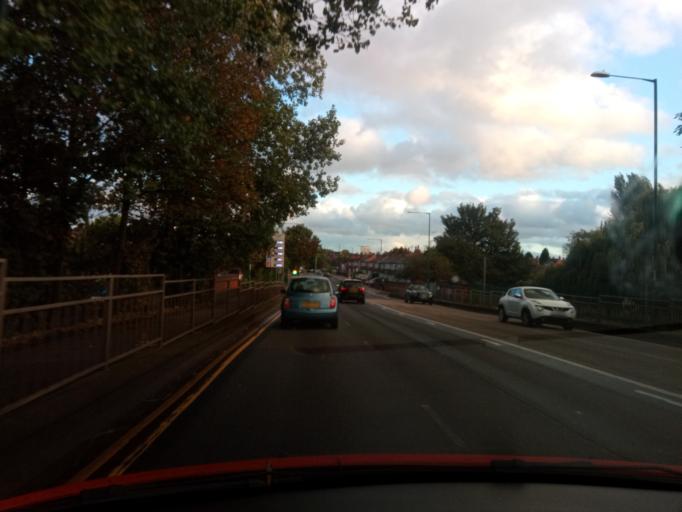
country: GB
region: England
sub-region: Nottingham
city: Nottingham
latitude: 52.9665
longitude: -1.1826
